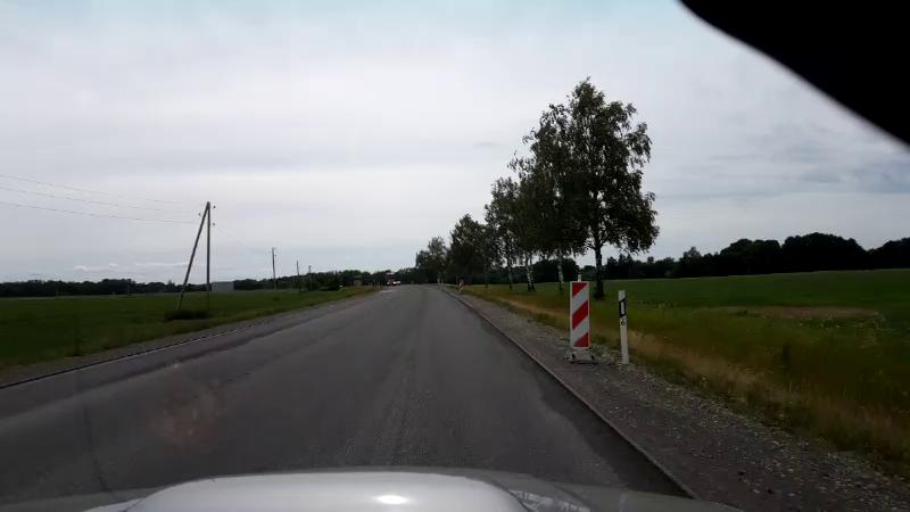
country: LV
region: Bauskas Rajons
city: Bauska
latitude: 56.3320
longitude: 24.2997
